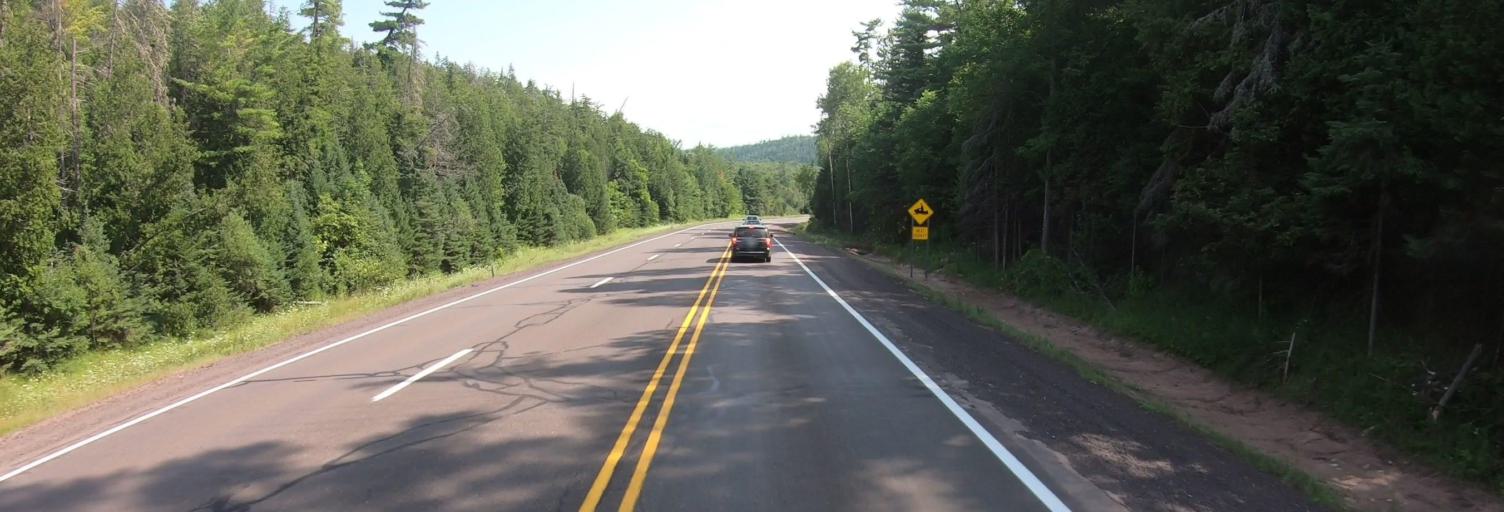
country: US
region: Michigan
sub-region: Ontonagon County
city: Ontonagon
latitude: 46.7053
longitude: -89.1594
